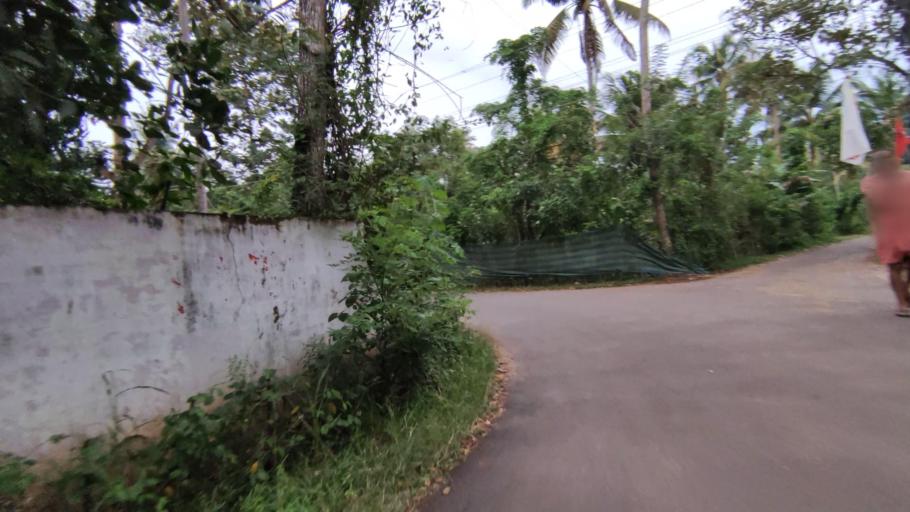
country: IN
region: Kerala
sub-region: Alappuzha
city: Shertallai
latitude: 9.6653
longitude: 76.3656
